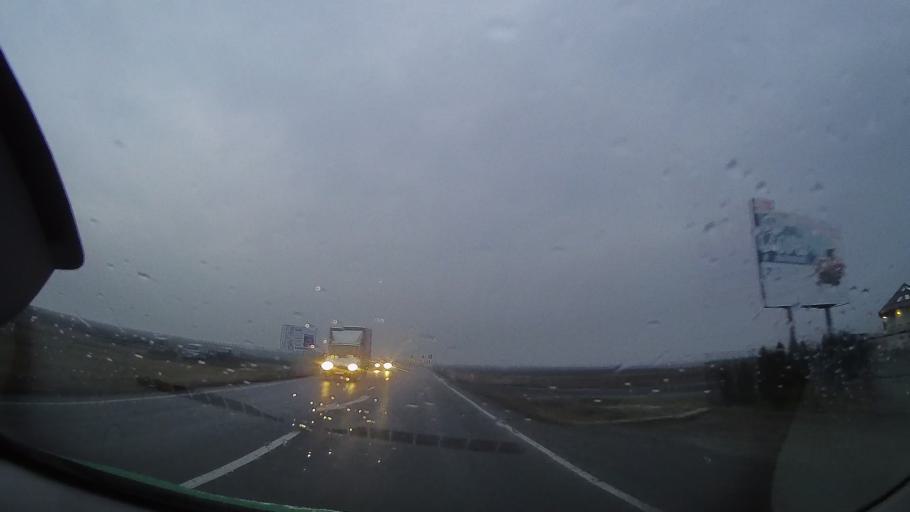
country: RO
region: Harghita
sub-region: Municipiul Gheorgheni
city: Gheorgheni
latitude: 46.7291
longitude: 25.5783
